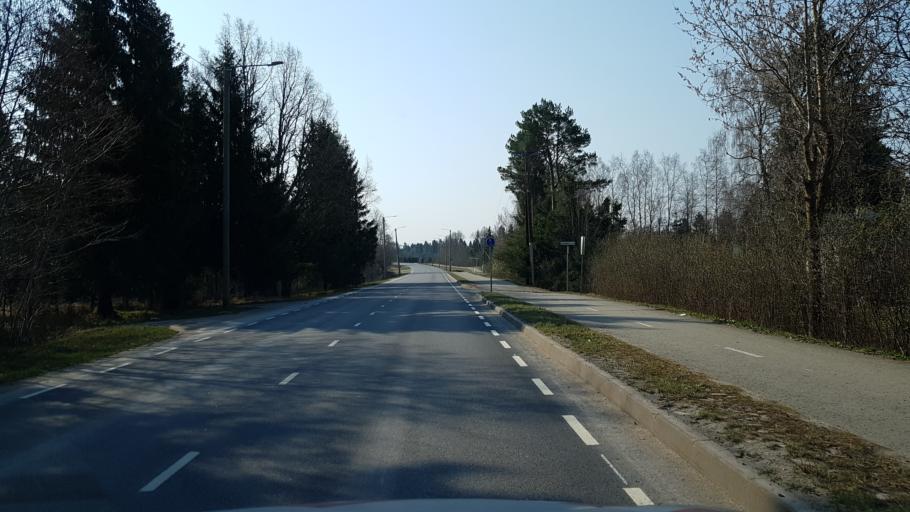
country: EE
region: Harju
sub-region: Saku vald
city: Saku
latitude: 59.2123
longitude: 24.6618
